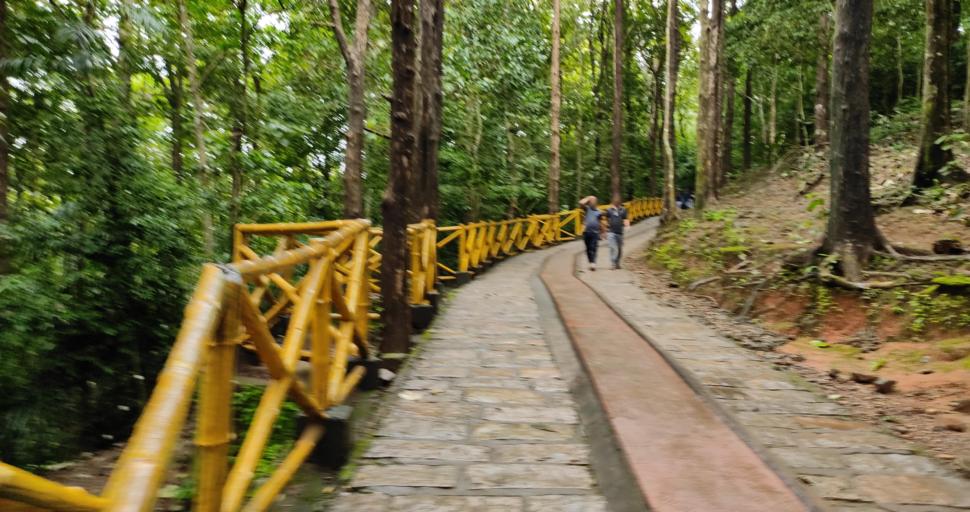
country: IN
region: Kerala
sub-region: Ernakulam
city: Angamali
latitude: 10.2886
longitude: 76.5697
